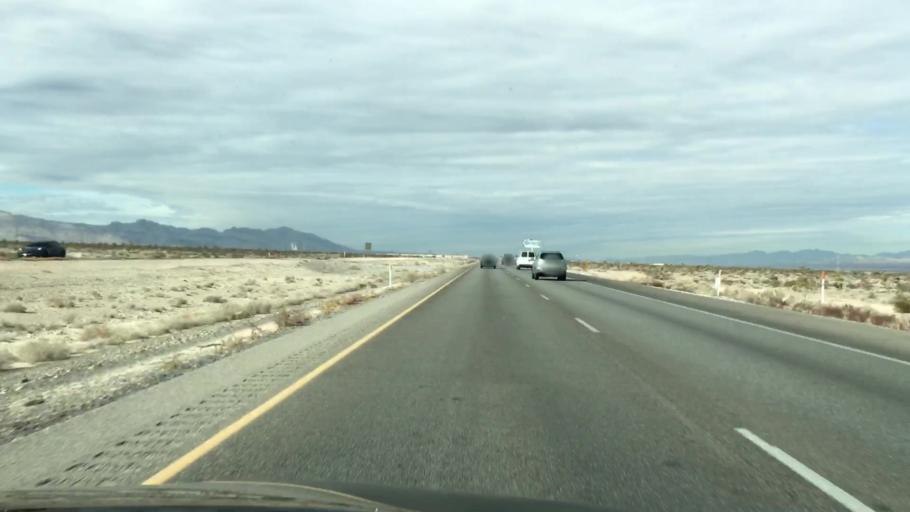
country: US
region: Nevada
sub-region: Clark County
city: Summerlin South
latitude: 36.3456
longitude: -115.3310
